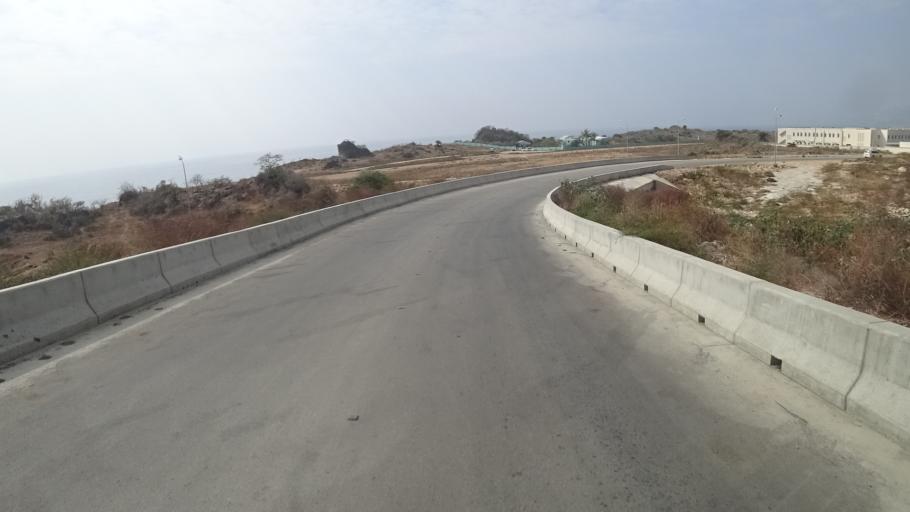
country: YE
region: Al Mahrah
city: Hawf
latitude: 16.7085
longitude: 53.2591
